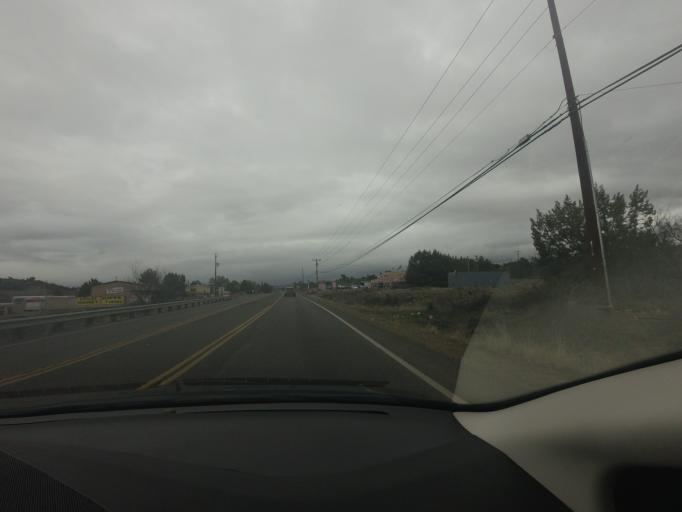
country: US
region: Arizona
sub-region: Yavapai County
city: Lake Montezuma
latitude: 34.6409
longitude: -111.7973
